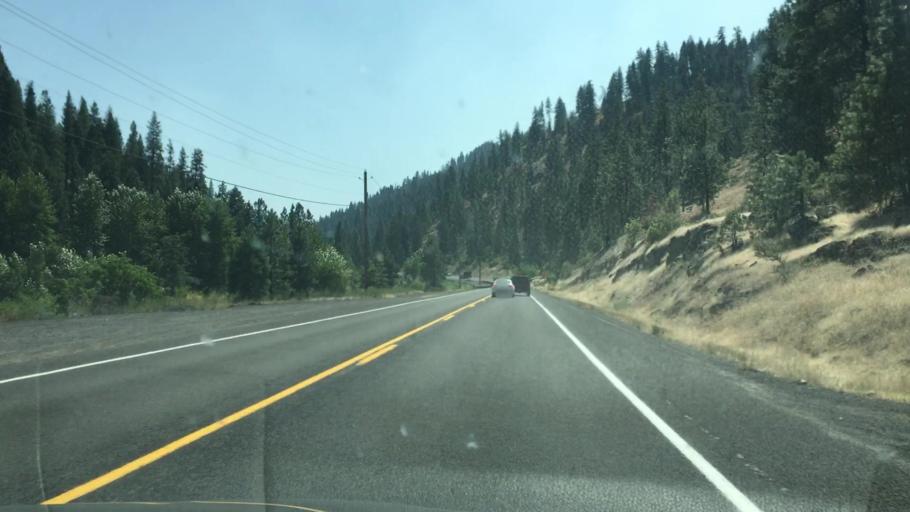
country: US
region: Idaho
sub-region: Valley County
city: McCall
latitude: 45.2088
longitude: -116.3131
